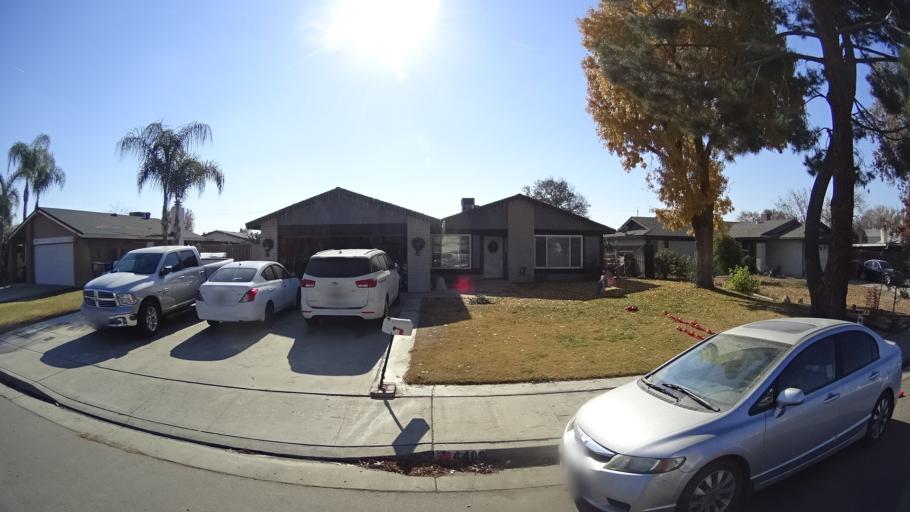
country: US
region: California
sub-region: Kern County
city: Greenfield
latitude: 35.2978
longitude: -119.0514
